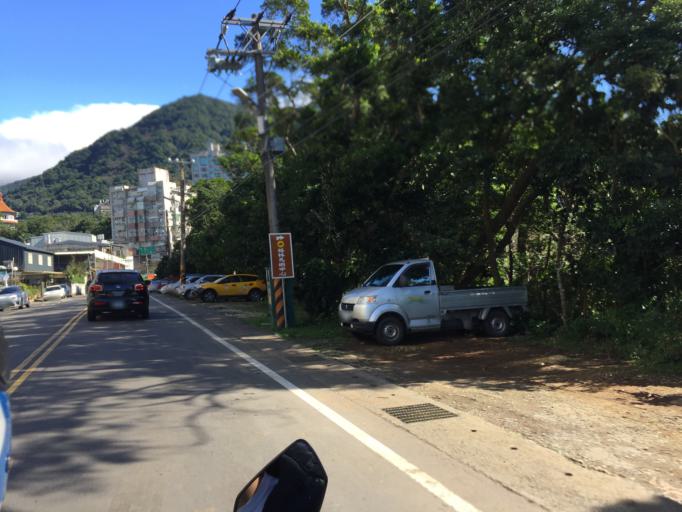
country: TW
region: Taipei
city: Taipei
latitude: 25.1856
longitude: 121.4804
